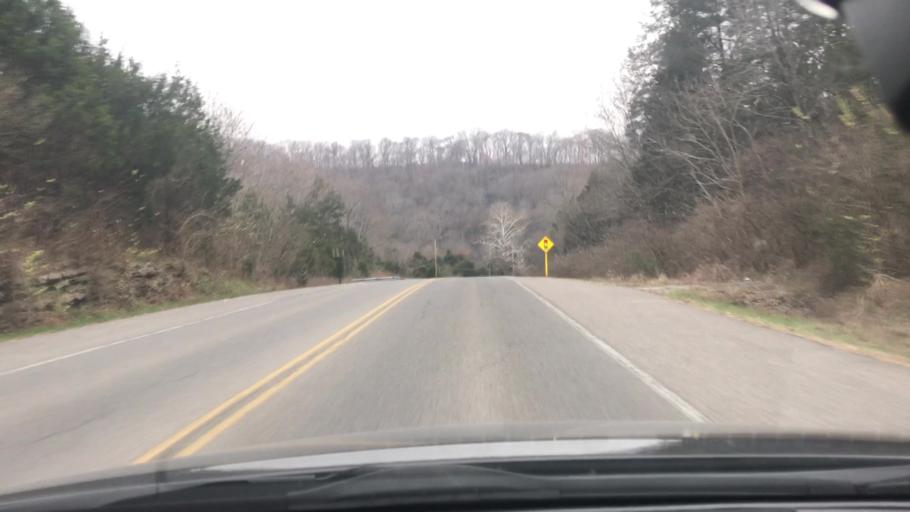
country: US
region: Tennessee
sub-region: Davidson County
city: Forest Hills
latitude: 36.0306
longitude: -86.8721
